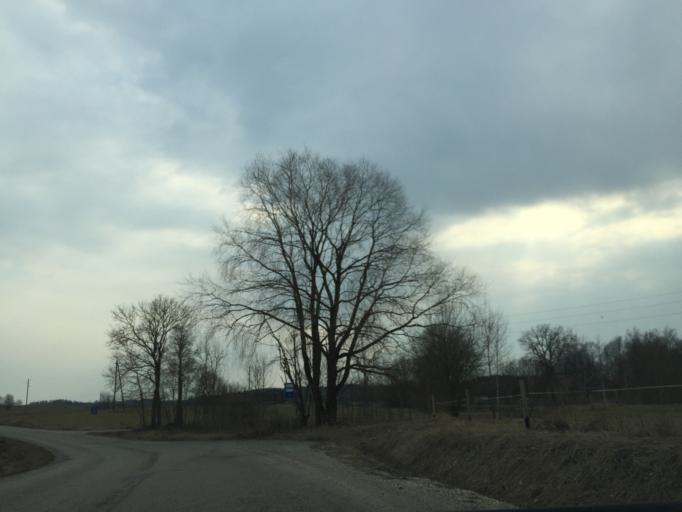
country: LV
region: Priekuli
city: Priekuli
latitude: 57.2453
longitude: 25.3725
